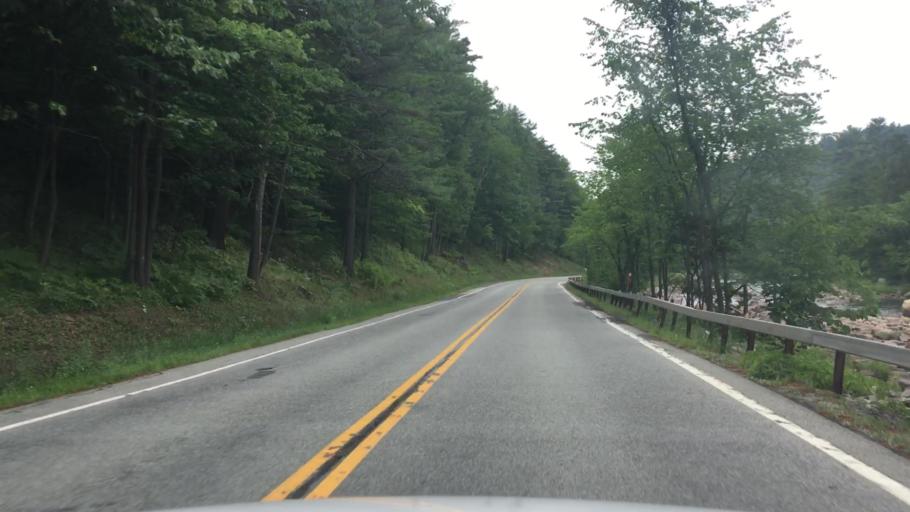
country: US
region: New York
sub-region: Essex County
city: Keeseville
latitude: 44.4230
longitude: -73.6814
